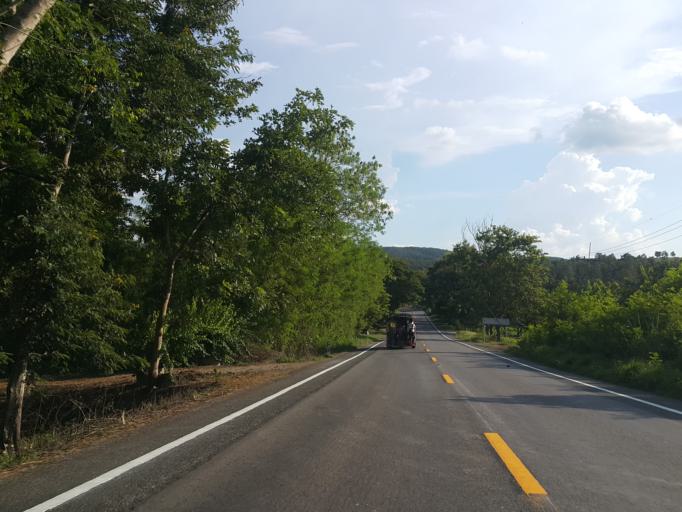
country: TH
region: Chiang Mai
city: Mae Taeng
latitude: 19.1037
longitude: 99.0004
